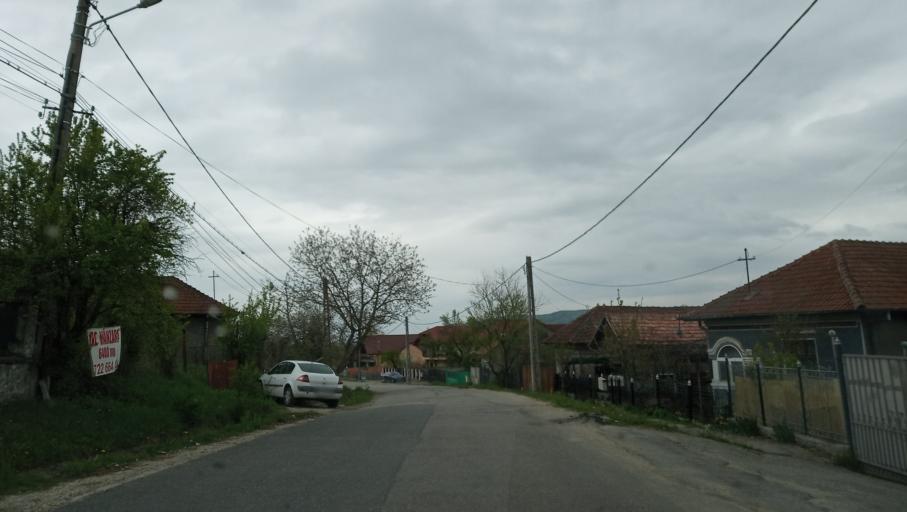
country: RO
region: Valcea
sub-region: Municipiul Ramnicu Valcea
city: Goranu
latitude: 45.1129
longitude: 24.3967
